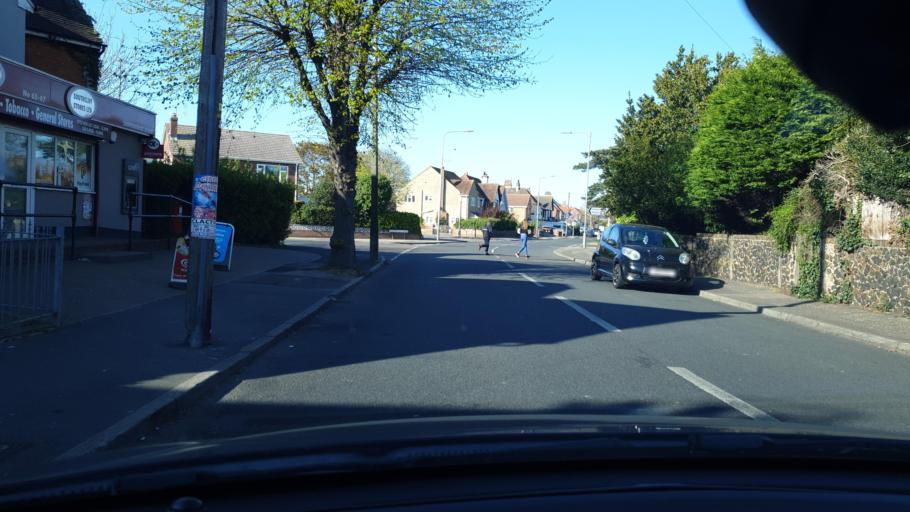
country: GB
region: England
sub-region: Essex
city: Clacton-on-Sea
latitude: 51.7936
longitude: 1.1616
